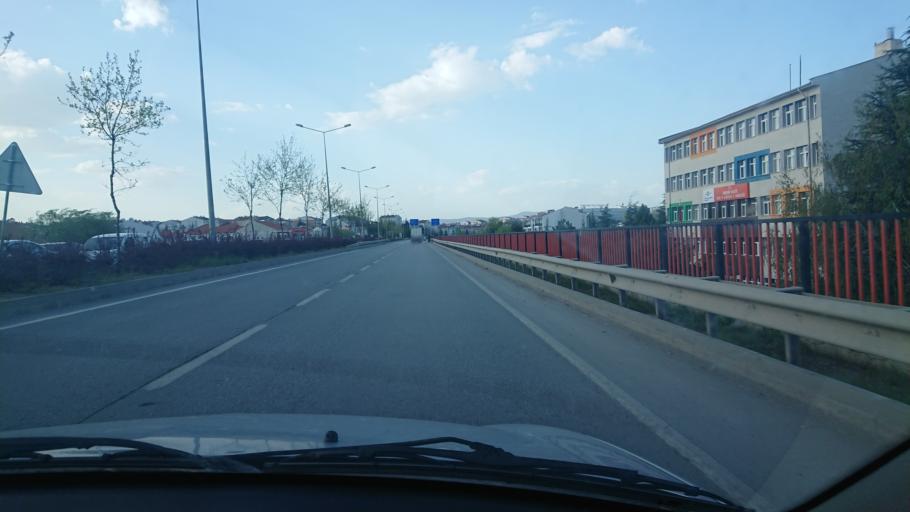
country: TR
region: Eskisehir
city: Eskisehir
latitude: 39.7780
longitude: 30.4841
